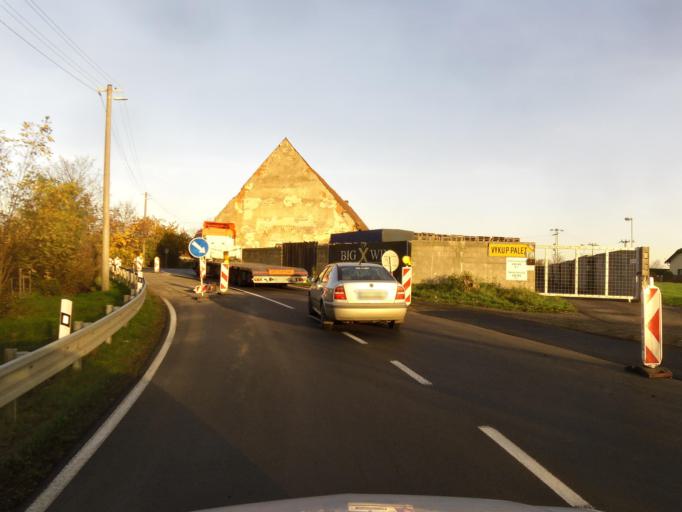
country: CZ
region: Liberecky
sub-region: Okres Ceska Lipa
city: Ceska Lipa
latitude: 50.6330
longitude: 14.5244
